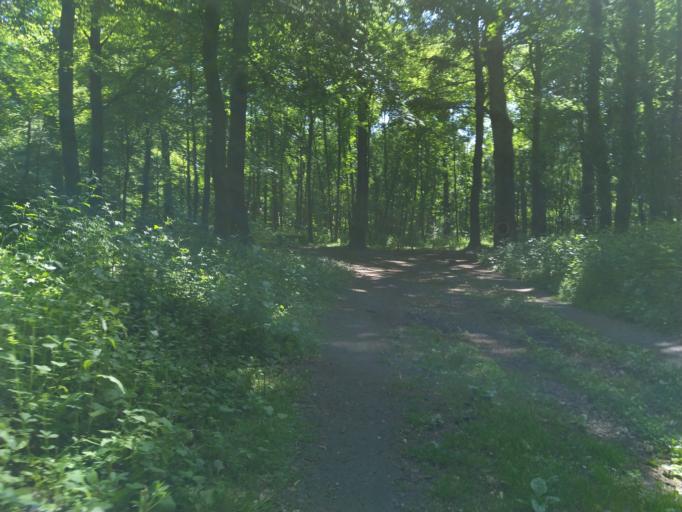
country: BE
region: Wallonia
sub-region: Province du Hainaut
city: Mons
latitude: 50.4600
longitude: 4.0252
